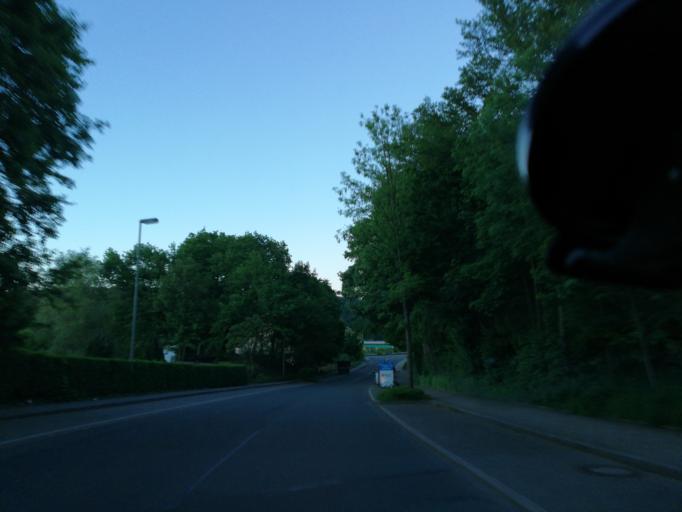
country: DE
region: North Rhine-Westphalia
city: Wetter (Ruhr)
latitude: 51.3872
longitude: 7.3736
